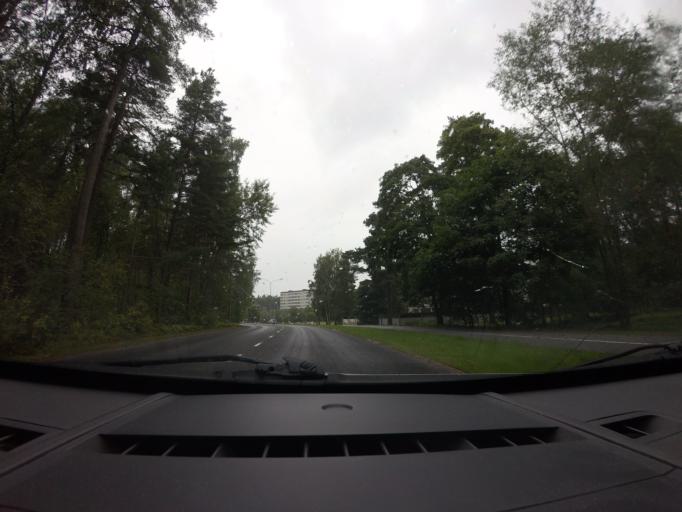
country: FI
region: Varsinais-Suomi
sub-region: Turku
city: Turku
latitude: 60.4311
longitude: 22.2875
